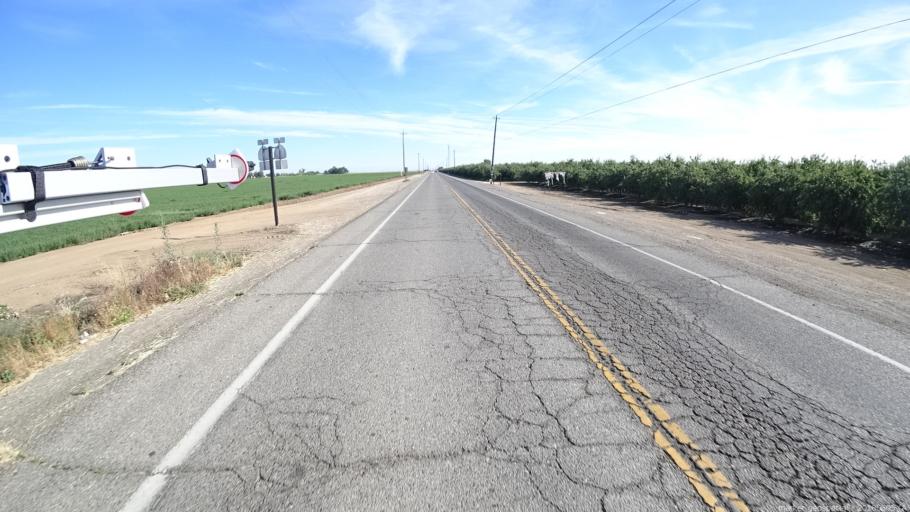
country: US
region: California
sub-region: Madera County
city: Chowchilla
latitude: 37.1442
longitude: -120.2745
